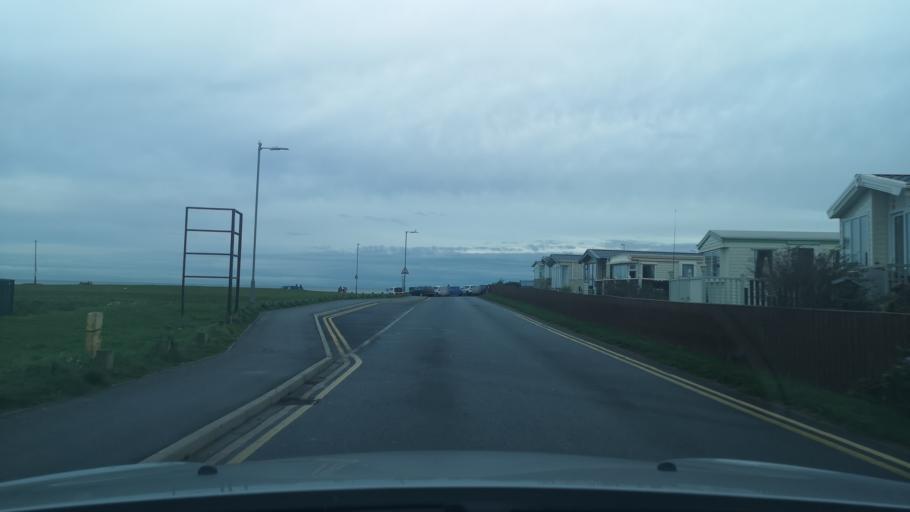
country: GB
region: England
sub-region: East Riding of Yorkshire
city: Hornsea
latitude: 53.9079
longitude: -0.1592
